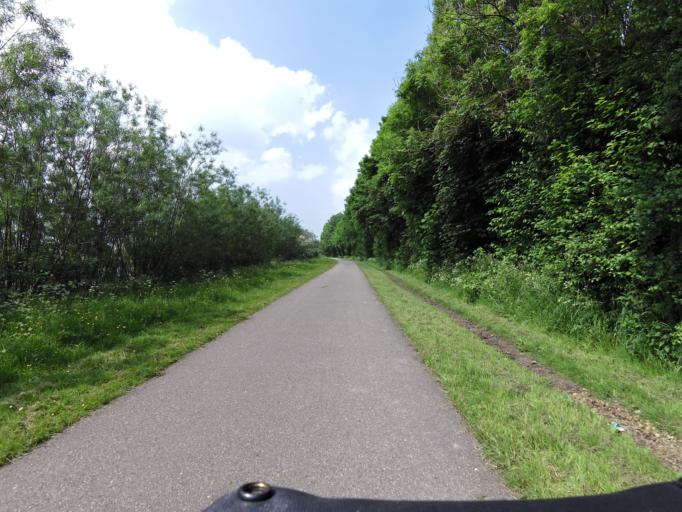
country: NL
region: South Holland
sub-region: Gemeente Spijkenisse
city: Spijkenisse
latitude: 51.8160
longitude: 4.2903
